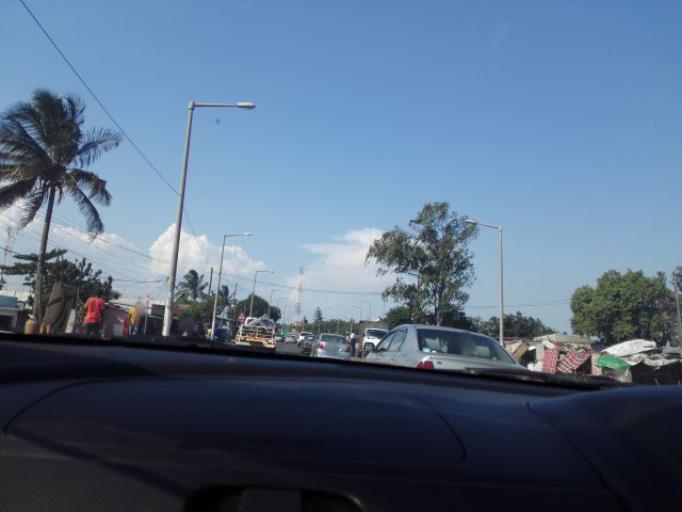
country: MZ
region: Maputo City
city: Maputo
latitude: -25.8838
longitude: 32.5668
